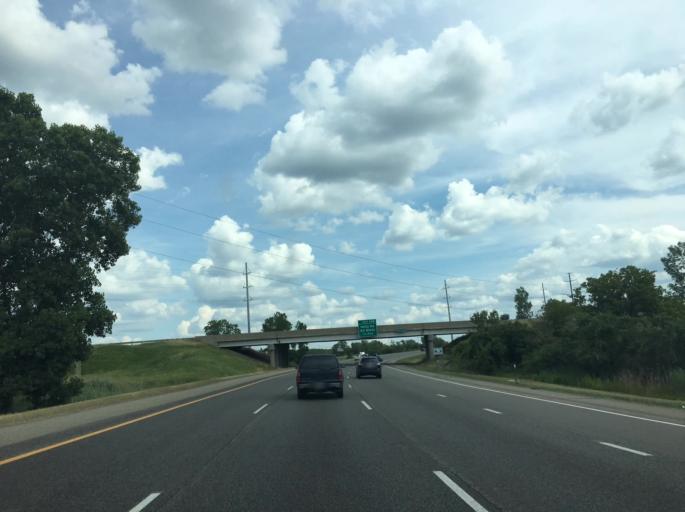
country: US
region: Michigan
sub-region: Genesee County
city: Grand Blanc
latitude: 42.9065
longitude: -83.6520
